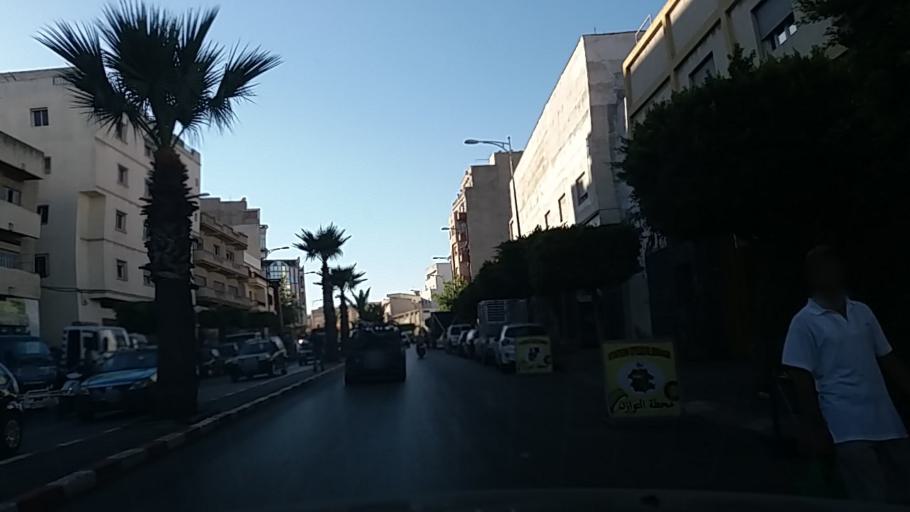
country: MA
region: Tanger-Tetouan
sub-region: Tanger-Assilah
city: Tangier
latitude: 35.7679
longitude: -5.8153
